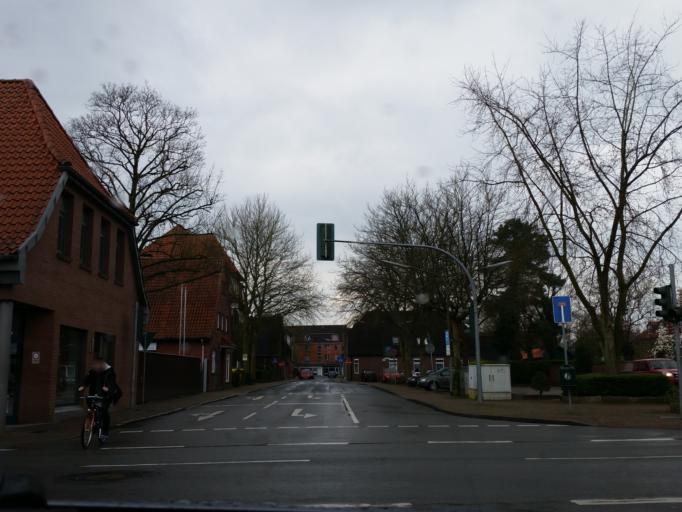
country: DE
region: Lower Saxony
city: Bremervorde
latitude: 53.4864
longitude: 9.1490
